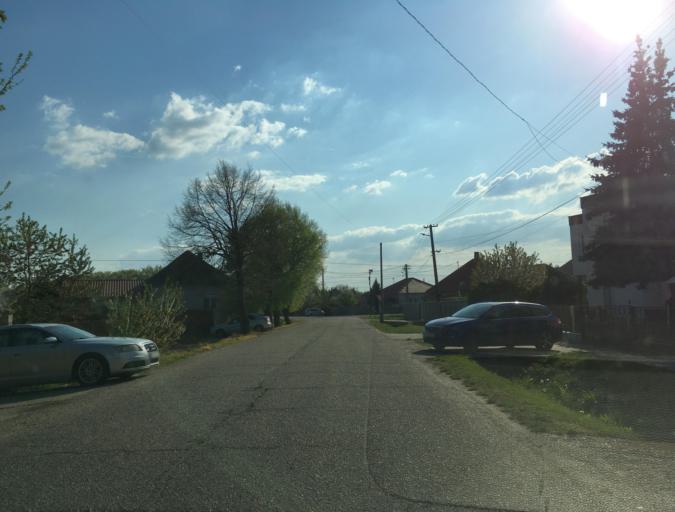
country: SK
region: Nitriansky
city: Kolarovo
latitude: 47.9098
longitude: 17.9973
